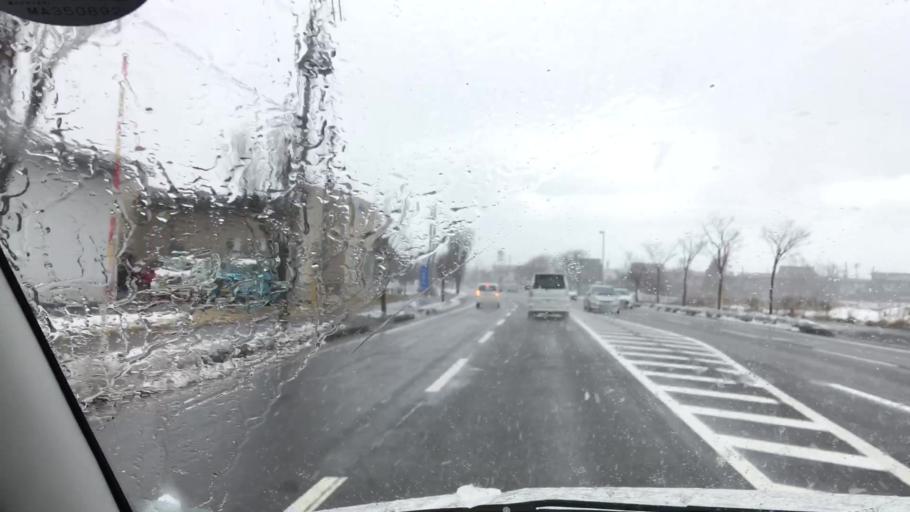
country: JP
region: Niigata
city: Joetsu
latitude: 37.1149
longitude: 138.2331
